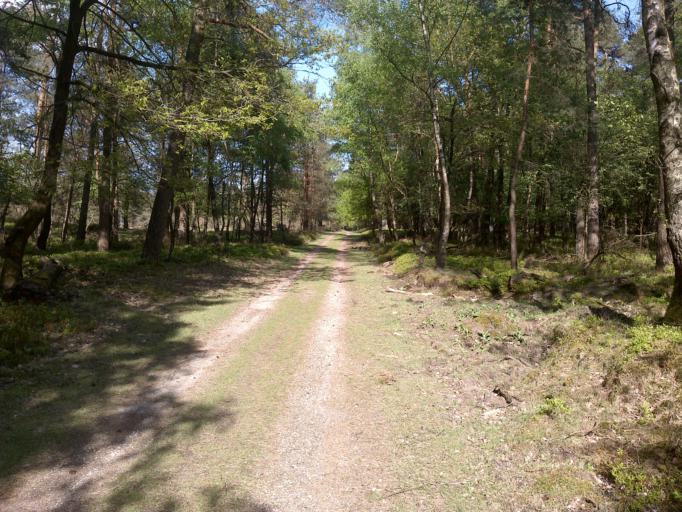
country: NL
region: Gelderland
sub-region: Gemeente Apeldoorn
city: Beekbergen
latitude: 52.0960
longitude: 5.9323
